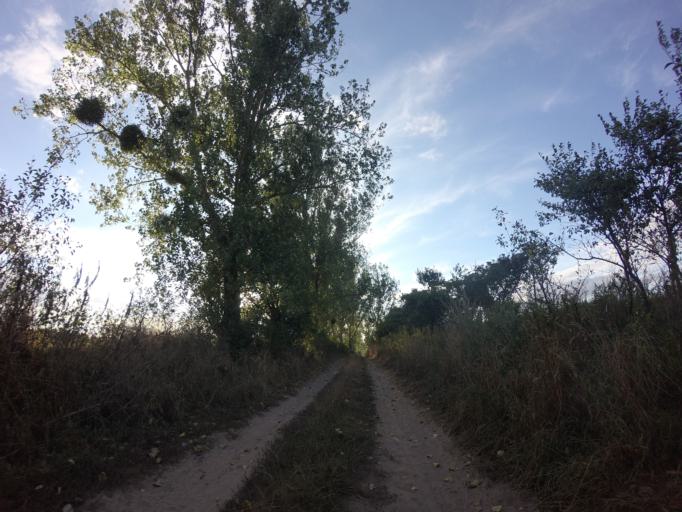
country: PL
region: West Pomeranian Voivodeship
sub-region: Powiat choszczenski
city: Choszczno
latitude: 53.1146
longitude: 15.4317
